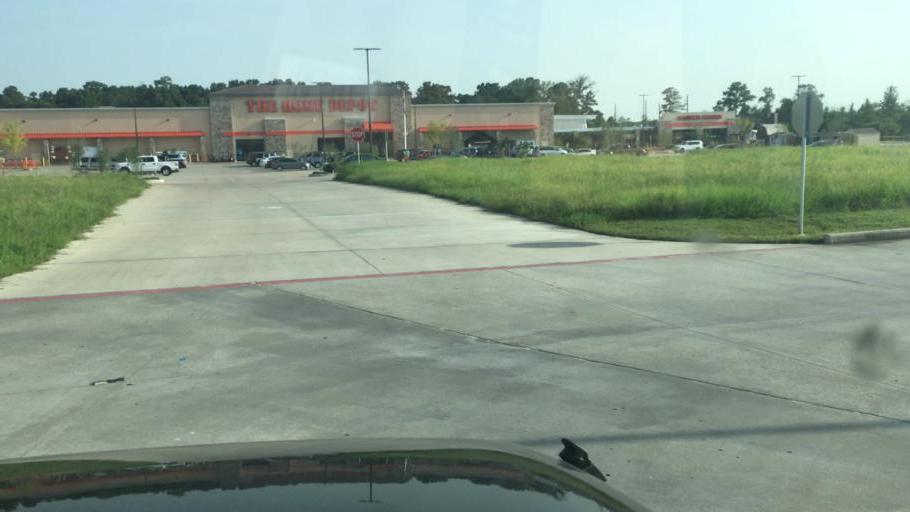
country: US
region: Texas
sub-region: Harris County
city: Atascocita
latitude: 29.9234
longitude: -95.1948
